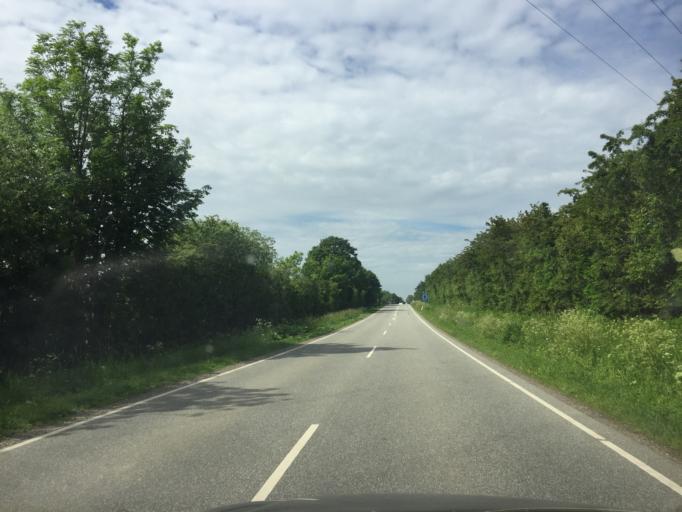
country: DK
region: South Denmark
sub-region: Kerteminde Kommune
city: Langeskov
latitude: 55.2231
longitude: 10.6173
